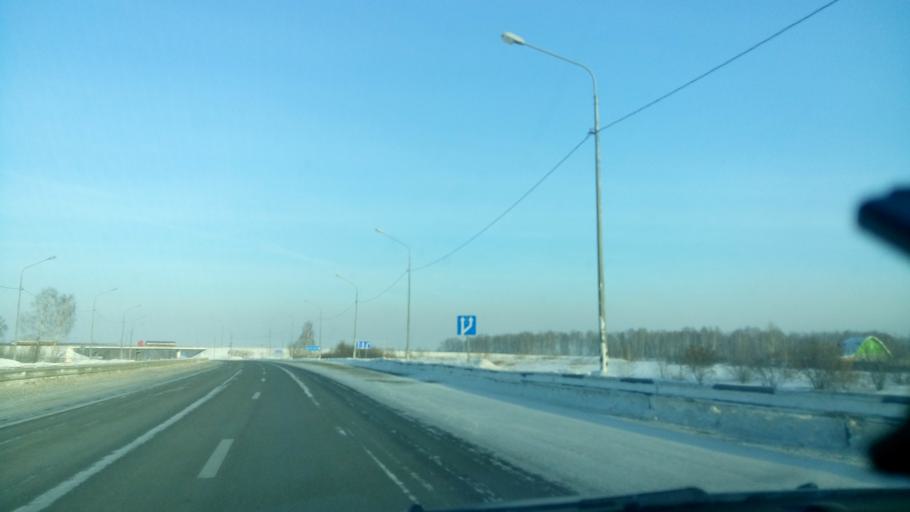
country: RU
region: Chelyabinsk
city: Dolgoderevenskoye
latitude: 55.3741
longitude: 61.3542
